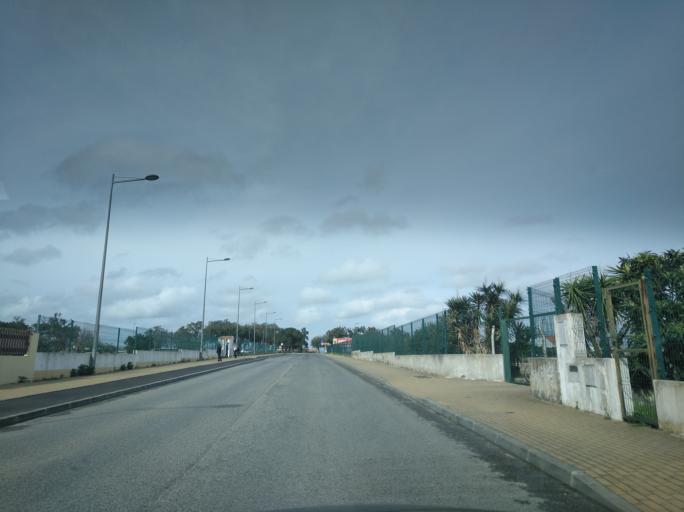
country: PT
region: Setubal
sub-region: Grandola
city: Grandola
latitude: 38.1864
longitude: -8.5634
